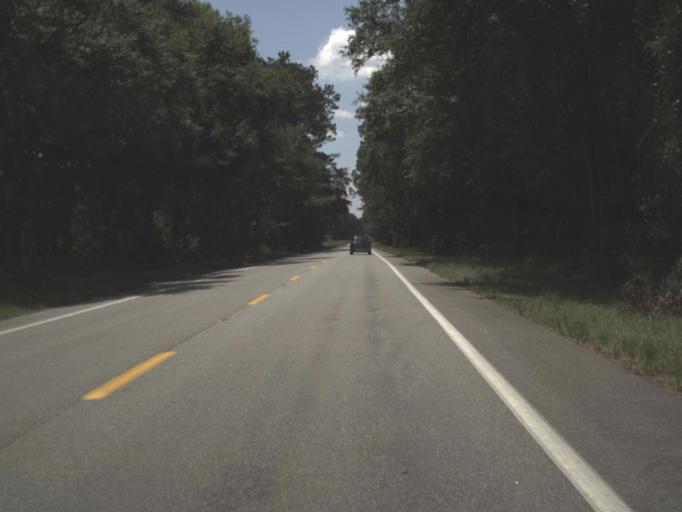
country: US
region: Florida
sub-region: Madison County
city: Madison
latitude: 30.5411
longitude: -83.6338
